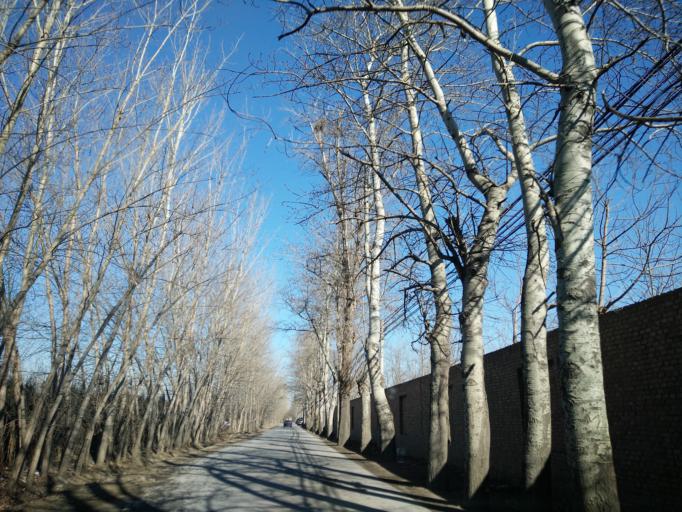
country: CN
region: Beijing
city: Yinghai
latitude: 39.7502
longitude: 116.4548
